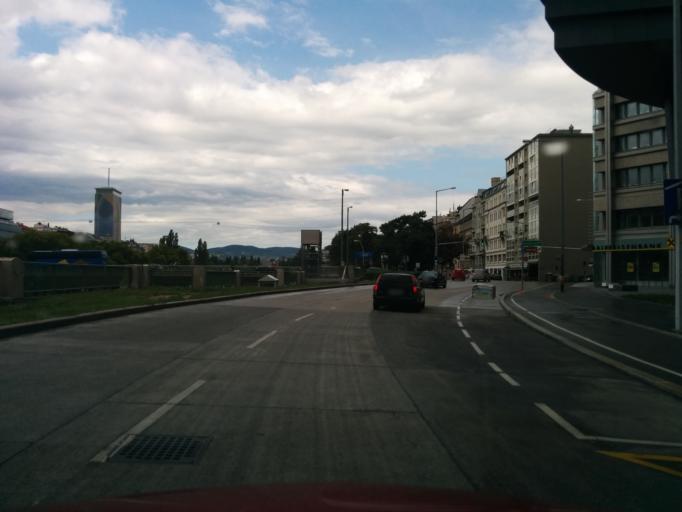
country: AT
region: Vienna
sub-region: Wien Stadt
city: Vienna
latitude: 48.2136
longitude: 16.3761
